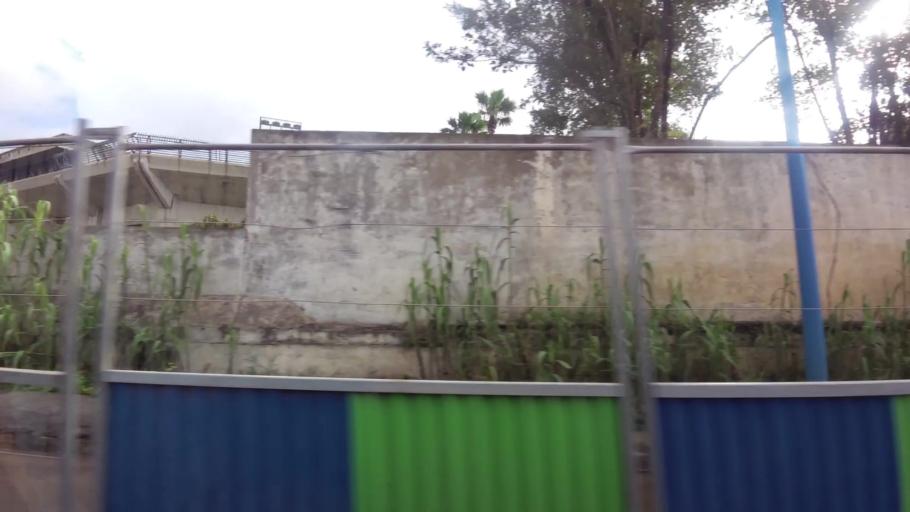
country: MA
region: Grand Casablanca
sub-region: Casablanca
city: Casablanca
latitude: 33.5547
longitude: -7.6495
